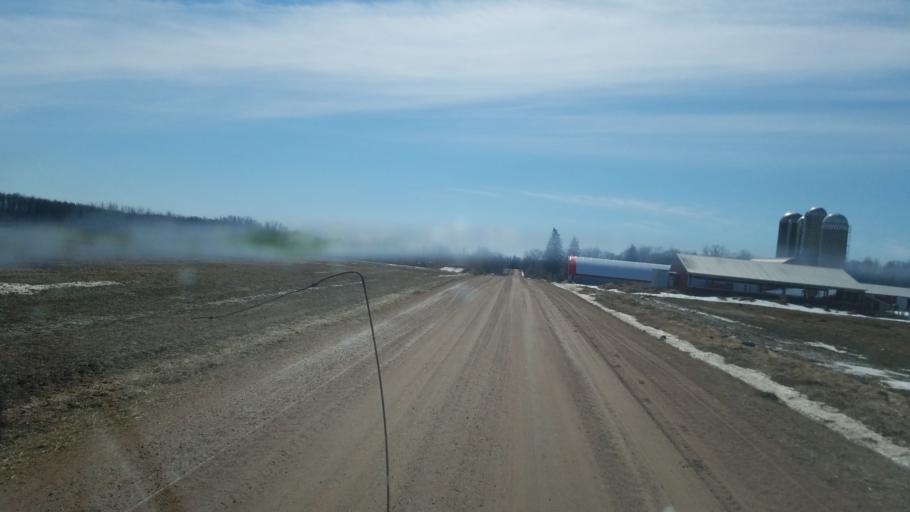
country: US
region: Wisconsin
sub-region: Clark County
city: Loyal
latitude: 44.6354
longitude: -90.4073
